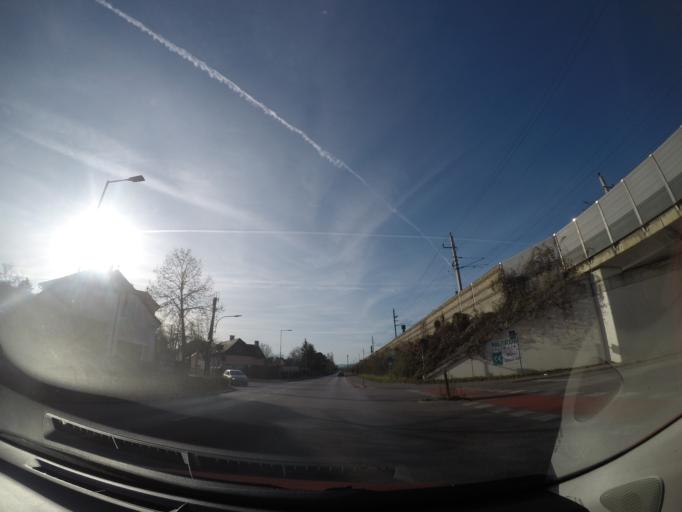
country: AT
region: Lower Austria
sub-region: Politischer Bezirk Baden
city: Pfaffstatten
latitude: 48.0109
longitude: 16.2510
